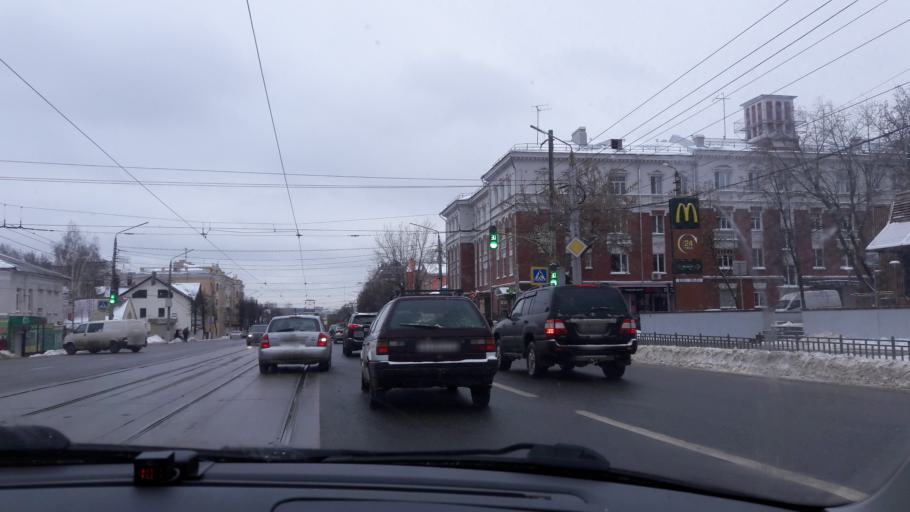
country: RU
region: Tula
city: Tula
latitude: 54.2106
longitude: 37.6212
